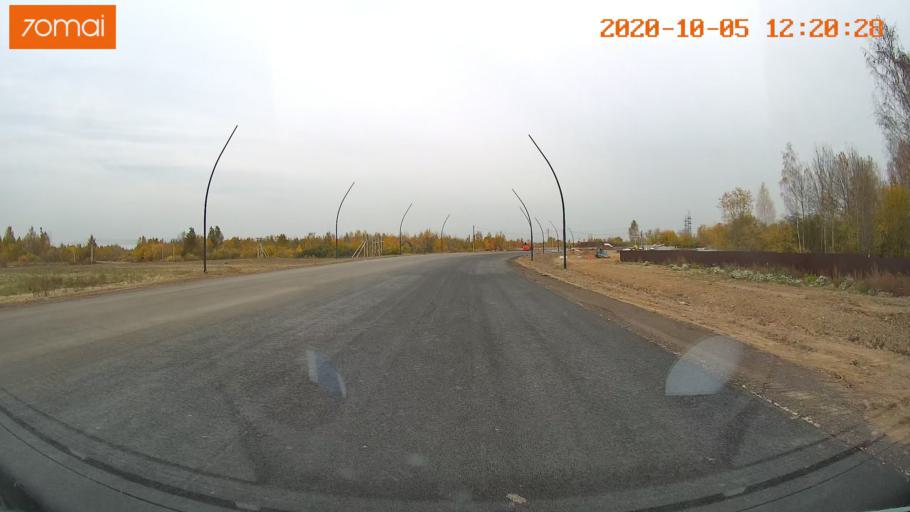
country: RU
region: Ivanovo
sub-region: Gorod Ivanovo
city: Ivanovo
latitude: 56.9637
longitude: 40.9307
